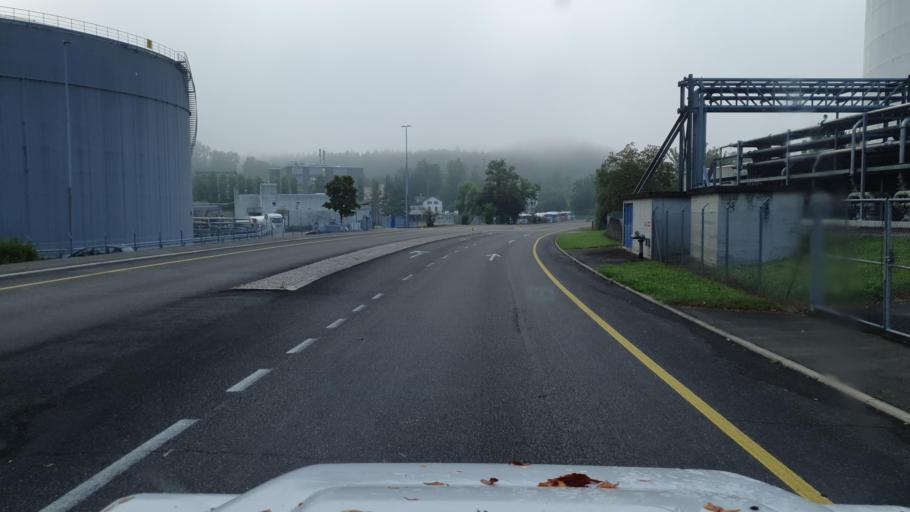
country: CH
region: Aargau
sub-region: Bezirk Baden
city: Mellingen
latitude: 47.4306
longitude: 8.2684
